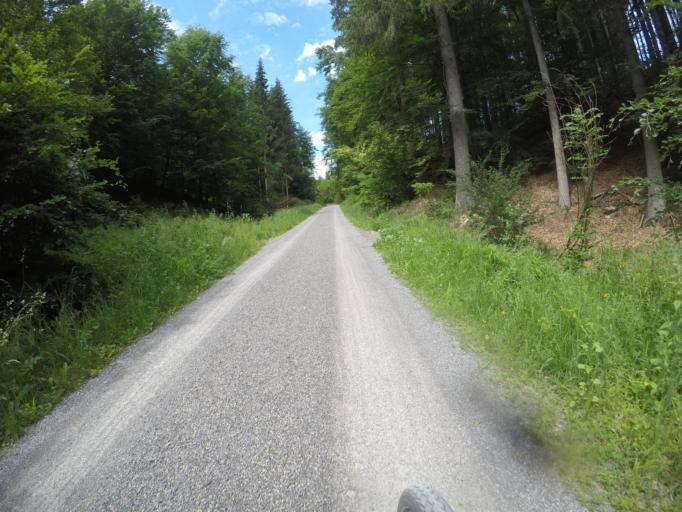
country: DE
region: Baden-Wuerttemberg
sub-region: Regierungsbezirk Stuttgart
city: Hildrizhausen
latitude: 48.6027
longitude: 8.9809
